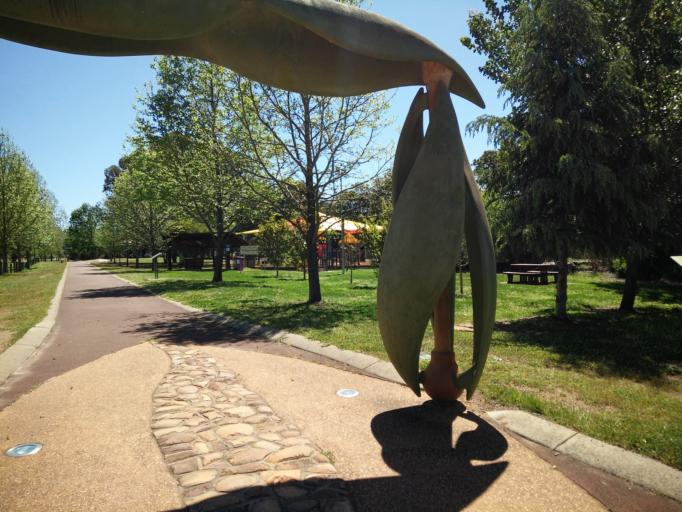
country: AU
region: Western Australia
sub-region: Bridgetown-Greenbushes
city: Bridgetown
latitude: -33.7857
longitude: 115.9843
